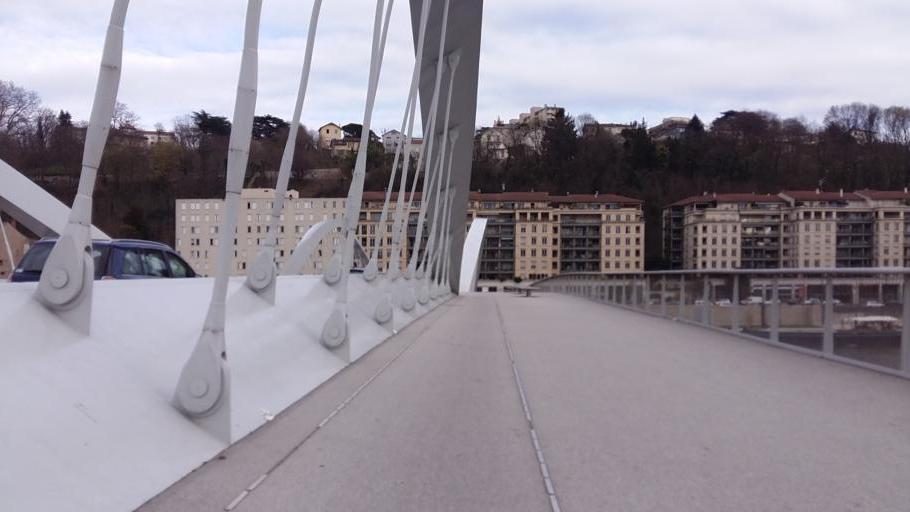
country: FR
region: Rhone-Alpes
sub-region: Departement du Rhone
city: Caluire-et-Cuire
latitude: 45.7803
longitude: 4.8097
